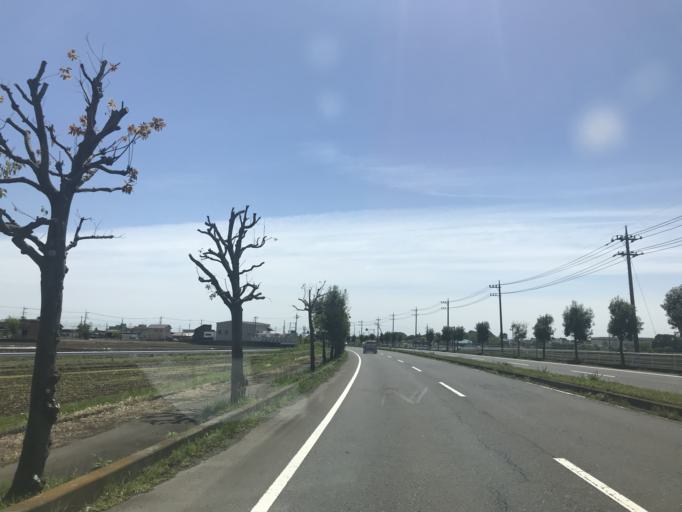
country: JP
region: Ibaraki
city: Shimodate
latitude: 36.2866
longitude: 139.9709
